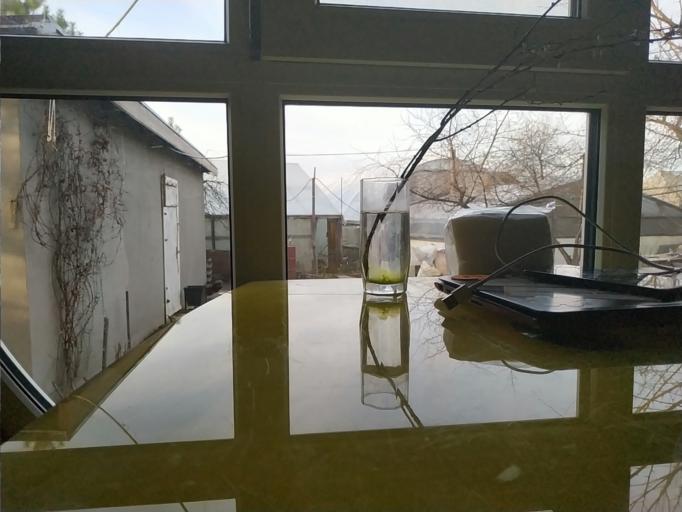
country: RU
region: Republic of Karelia
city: Suoyarvi
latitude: 62.1348
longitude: 32.1481
